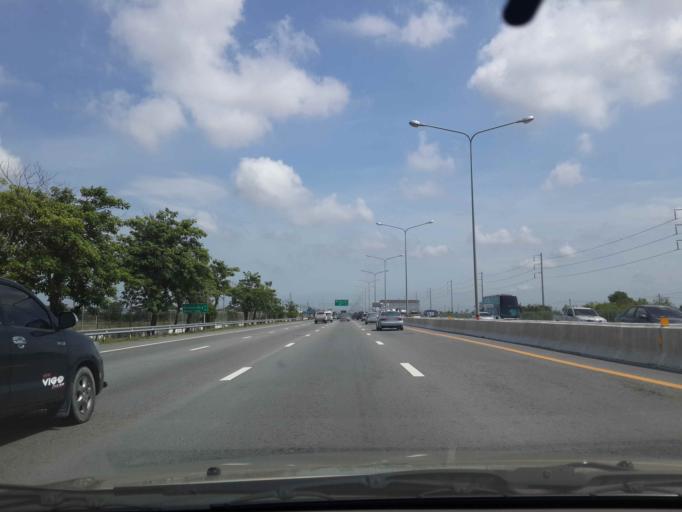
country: TH
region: Chachoengsao
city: Bang Pakong
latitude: 13.5810
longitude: 100.9737
